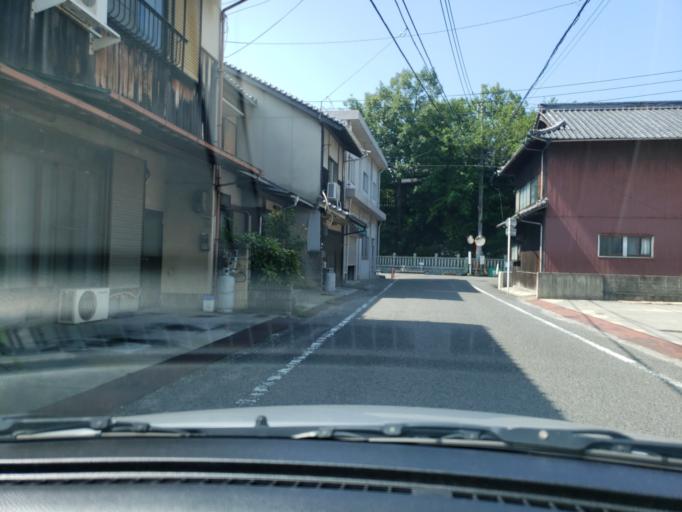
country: JP
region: Ehime
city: Hojo
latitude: 34.1065
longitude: 132.9671
